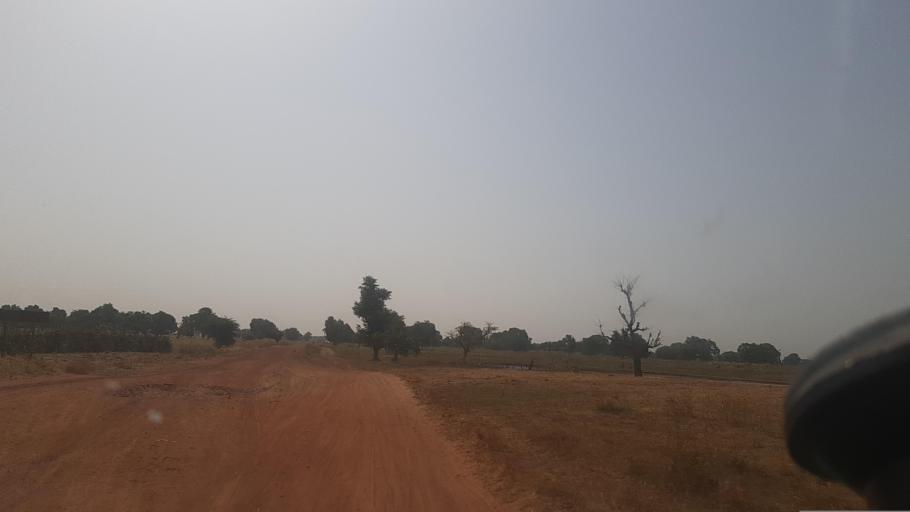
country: ML
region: Segou
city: Baroueli
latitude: 13.0069
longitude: -6.4207
